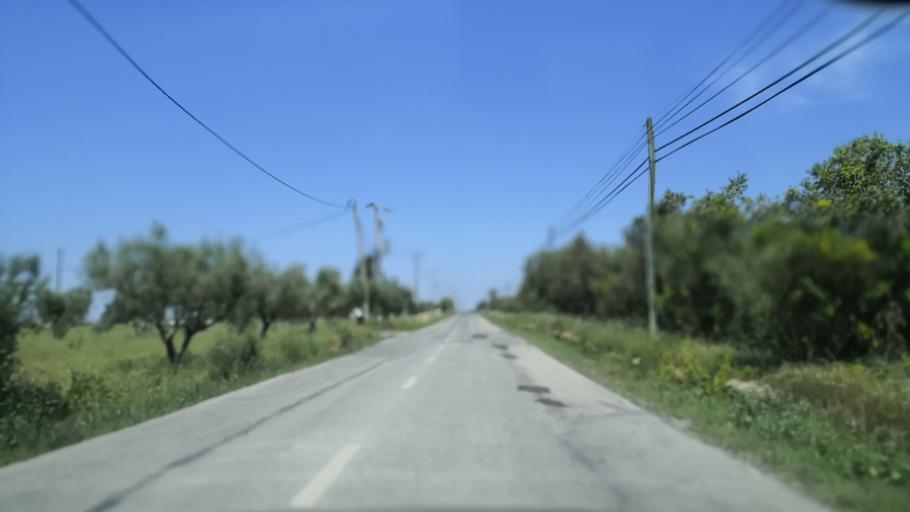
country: PT
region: Setubal
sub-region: Palmela
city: Pinhal Novo
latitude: 38.6528
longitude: -8.7425
